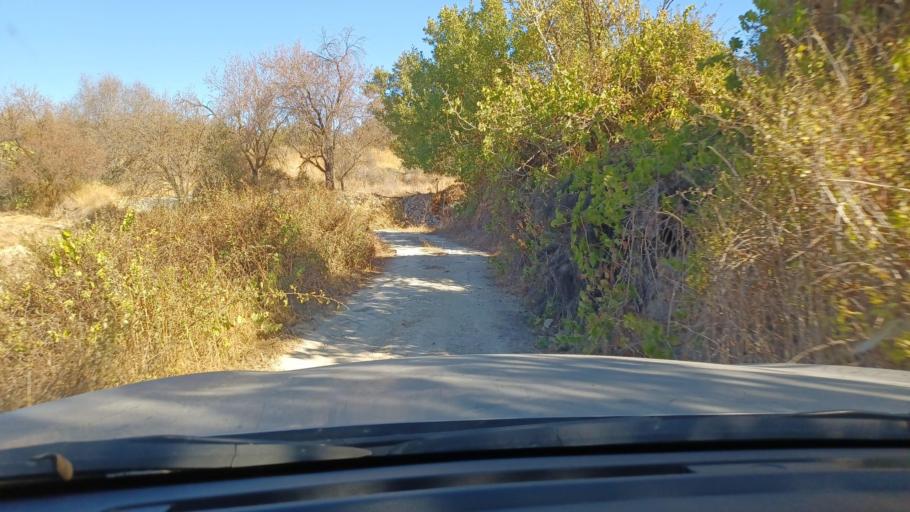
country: CY
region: Pafos
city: Polis
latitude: 35.0091
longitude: 32.5040
